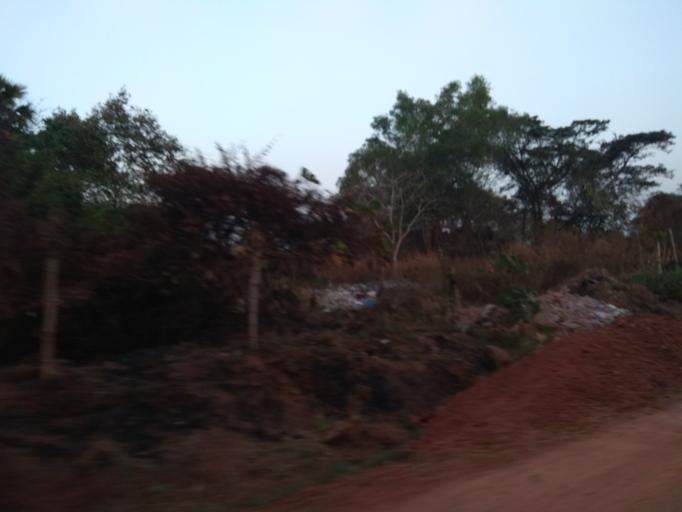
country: IN
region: Karnataka
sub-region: Dakshina Kannada
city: Mangalore
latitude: 12.9283
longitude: 74.8745
